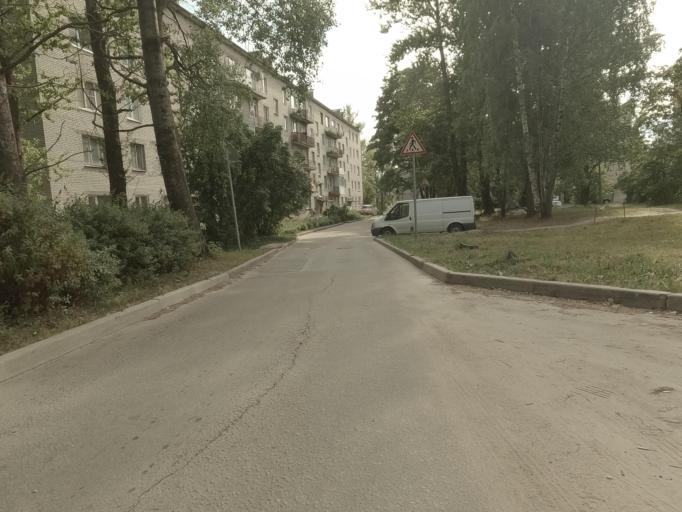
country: RU
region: Leningrad
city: Kamennogorsk
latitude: 60.9549
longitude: 29.1320
